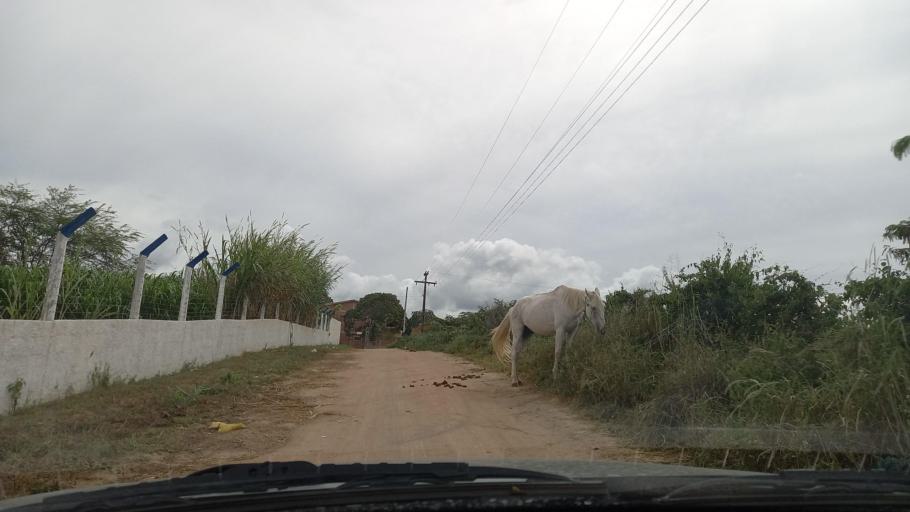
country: BR
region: Pernambuco
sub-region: Gravata
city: Gravata
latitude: -8.1915
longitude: -35.5984
